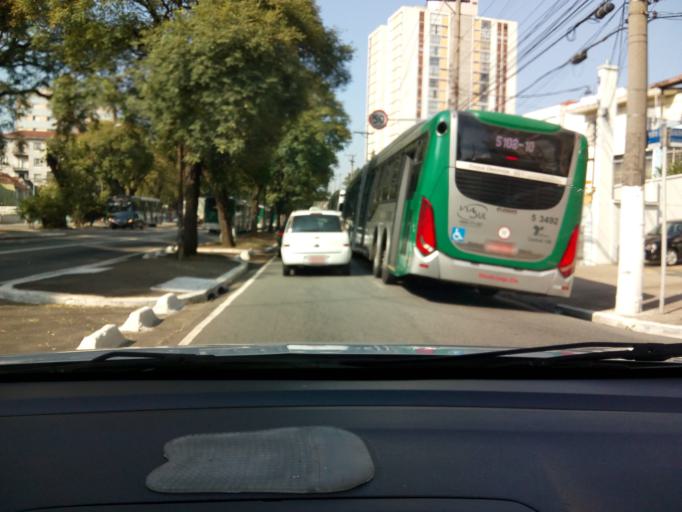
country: BR
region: Sao Paulo
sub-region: Sao Paulo
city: Sao Paulo
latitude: -23.5719
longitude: -46.6111
